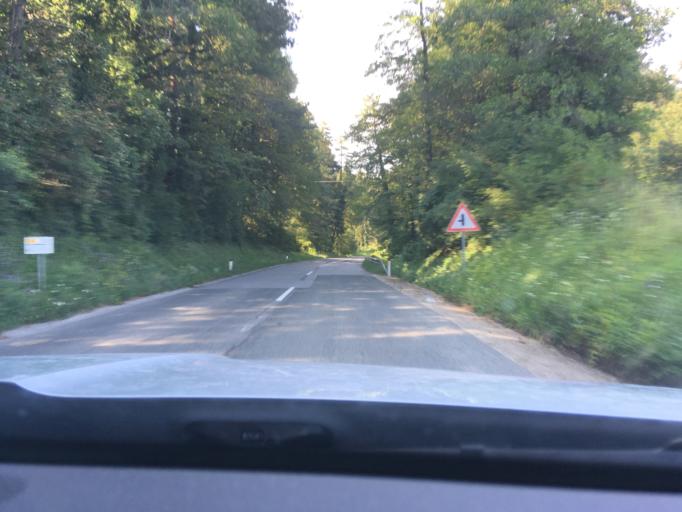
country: SI
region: Crnomelj
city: Crnomelj
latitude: 45.5495
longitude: 15.1614
